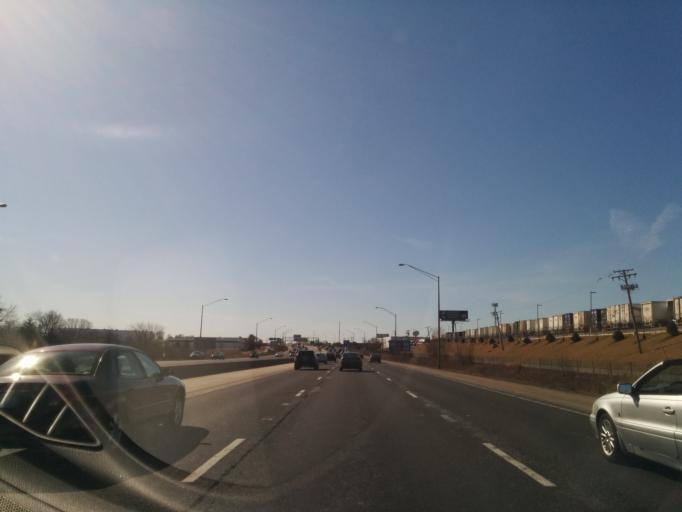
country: US
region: Illinois
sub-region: DuPage County
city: Burr Ridge
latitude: 41.7527
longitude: -87.9256
